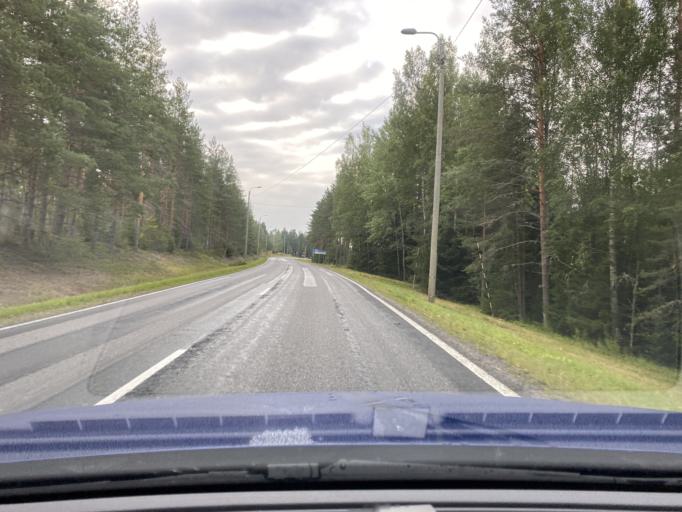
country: FI
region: Southern Ostrobothnia
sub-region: Seinaejoki
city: Jurva
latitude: 62.6782
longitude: 21.9781
